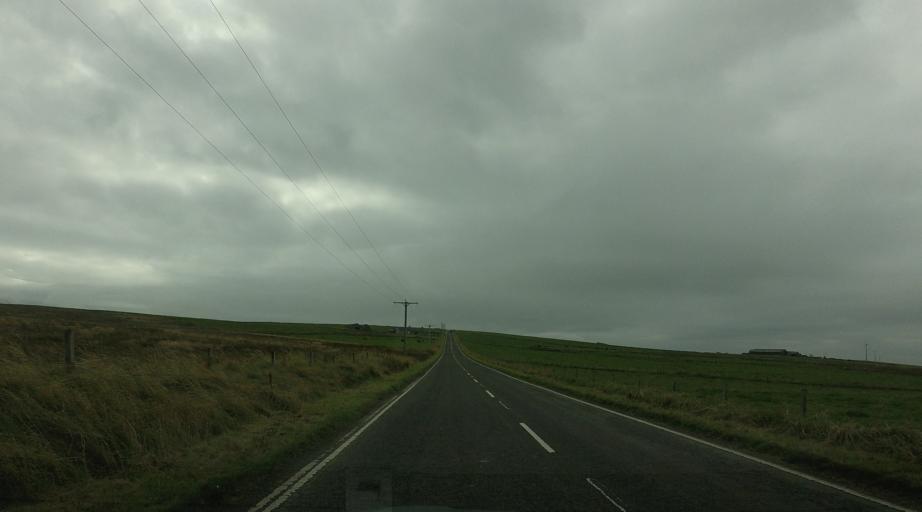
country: GB
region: Scotland
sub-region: Orkney Islands
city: Orkney
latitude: 58.7833
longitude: -2.9589
